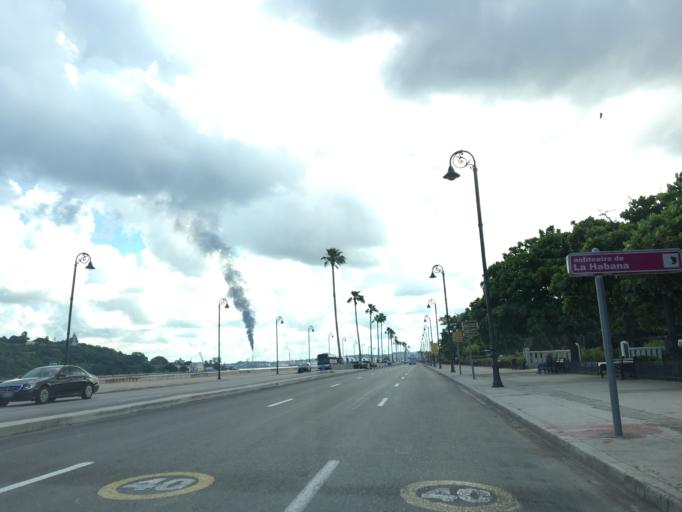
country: CU
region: La Habana
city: Centro Habana
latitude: 23.1442
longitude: -82.3535
